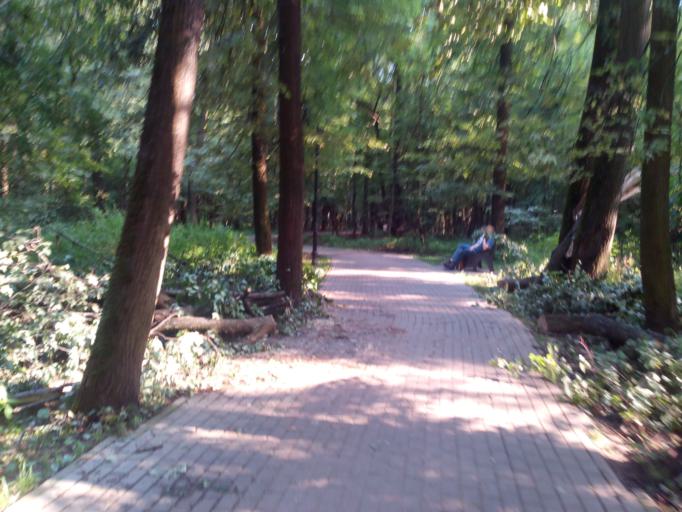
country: RU
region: Moskovskaya
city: Fili
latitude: 55.7481
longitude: 37.4857
